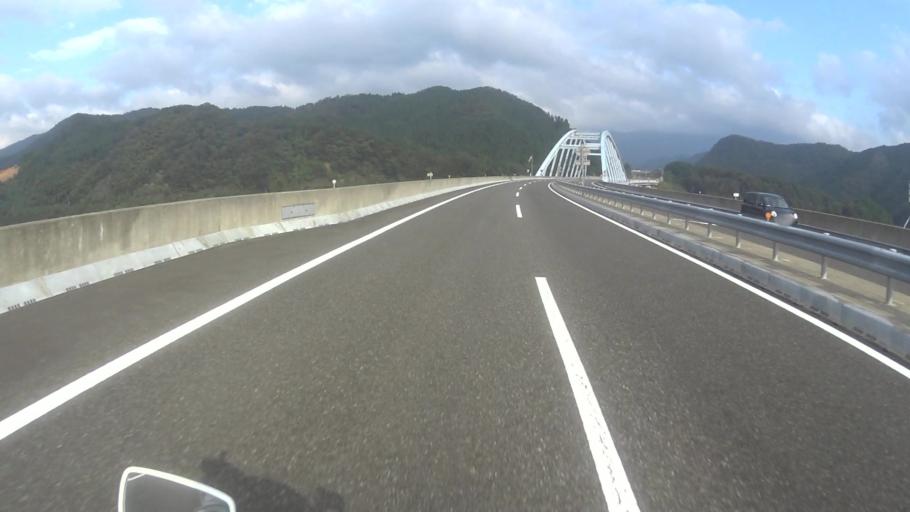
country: JP
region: Kyoto
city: Miyazu
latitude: 35.4200
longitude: 135.2132
